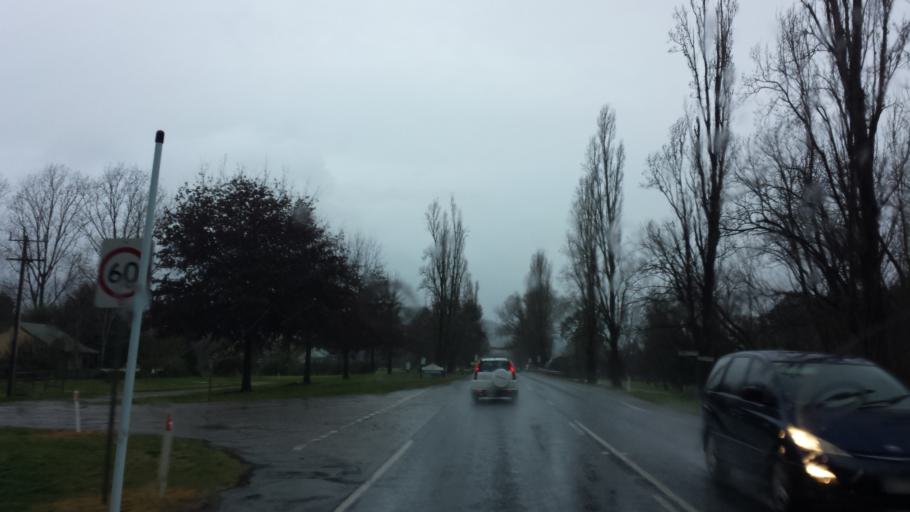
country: AU
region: Victoria
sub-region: Wangaratta
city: Wangaratta
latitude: -36.5527
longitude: 146.7106
